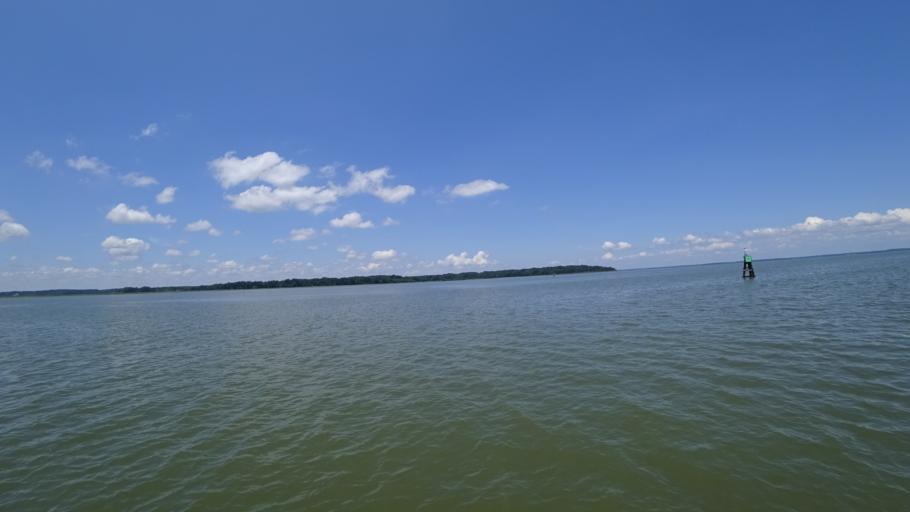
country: US
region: Virginia
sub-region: Isle of Wight County
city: Carrollton
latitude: 37.0027
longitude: -76.5732
